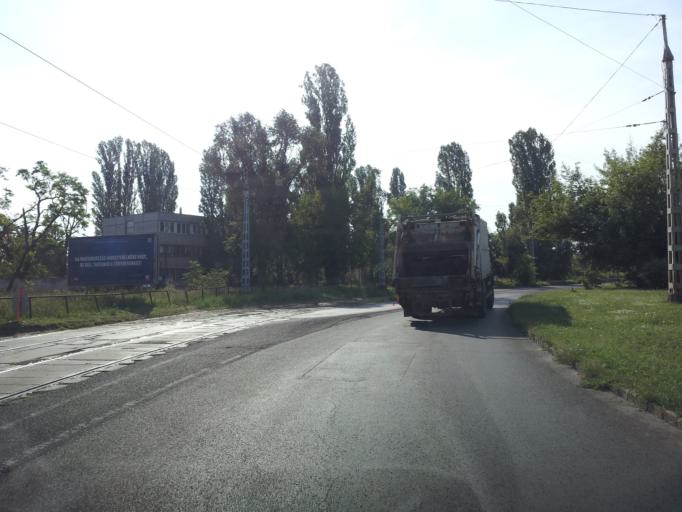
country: HU
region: Budapest
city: Budapest IX. keruelet
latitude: 47.4617
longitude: 19.0858
